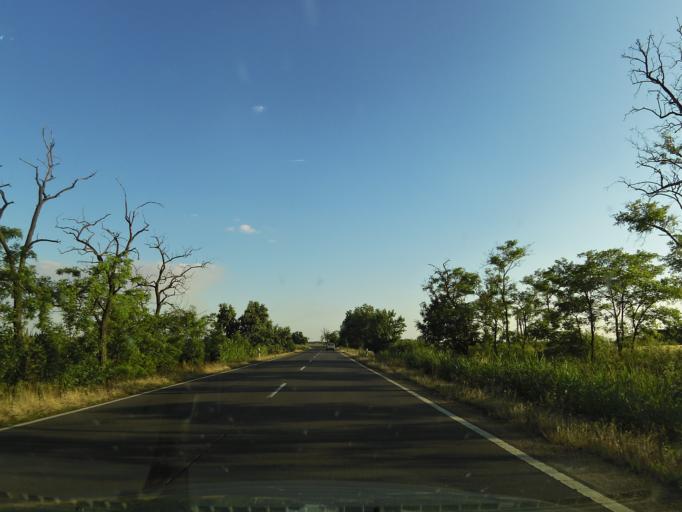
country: HU
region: Jasz-Nagykun-Szolnok
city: Kunszentmarton
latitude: 46.8782
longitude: 20.2664
